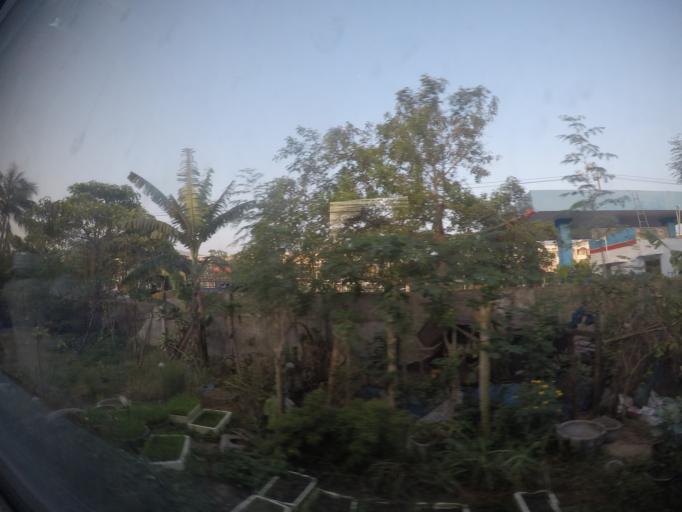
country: VN
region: Phu Yen
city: Tuy Hoa
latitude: 13.0976
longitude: 109.2926
